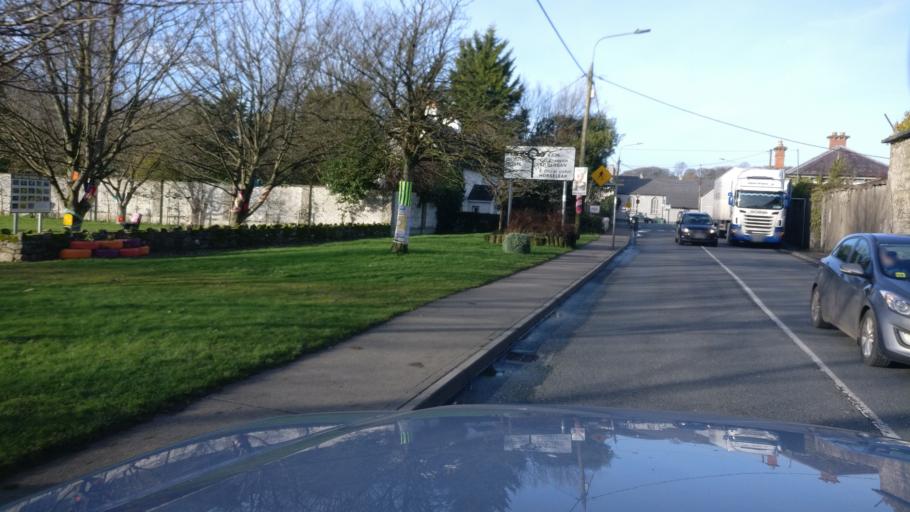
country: IE
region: Leinster
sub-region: Uibh Fhaili
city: Clara
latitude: 53.3401
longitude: -7.6093
